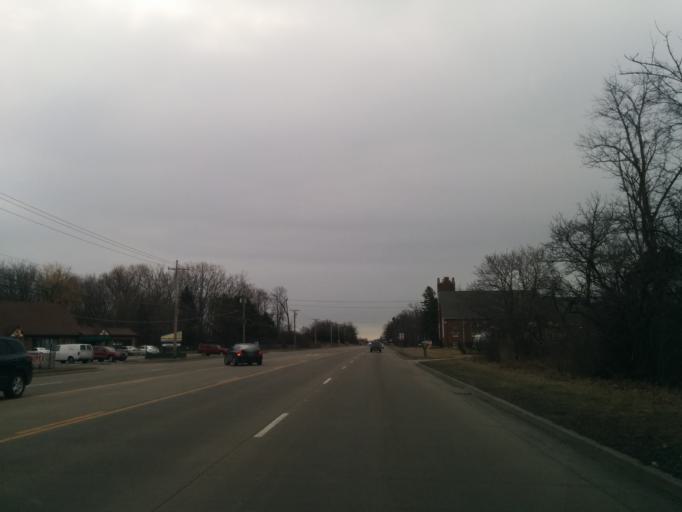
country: US
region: Illinois
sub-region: Cook County
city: Prospect Heights
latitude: 42.0994
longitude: -87.8823
